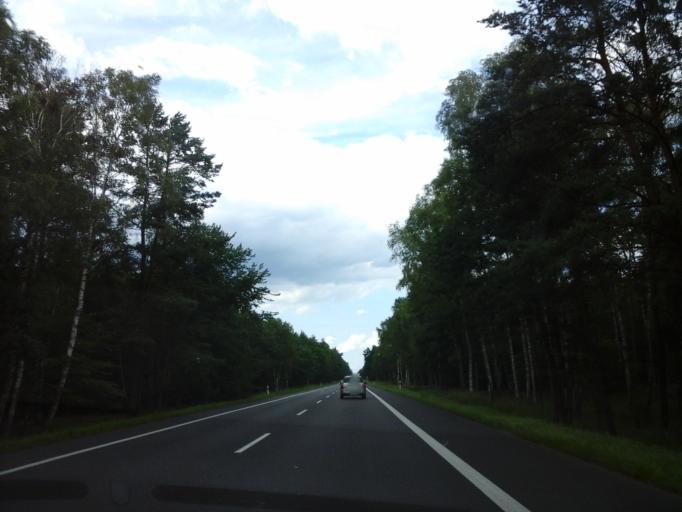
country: PL
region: West Pomeranian Voivodeship
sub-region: Powiat goleniowski
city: Goleniow
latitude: 53.6373
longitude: 14.8177
